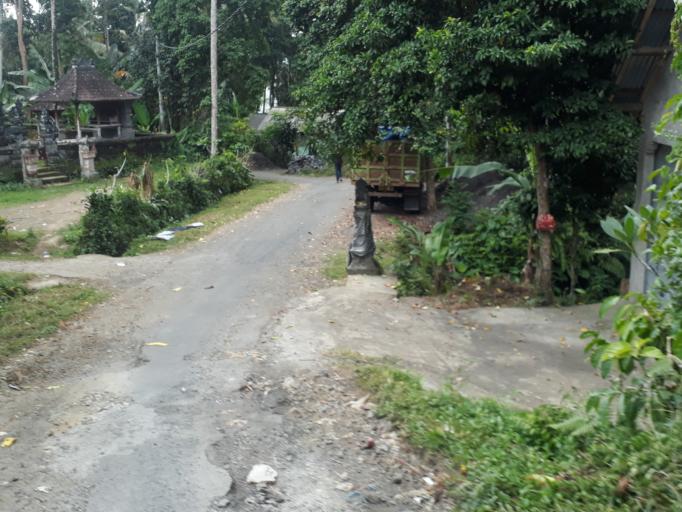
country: ID
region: Bali
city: Banjar Wangsian
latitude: -8.4598
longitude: 115.4375
